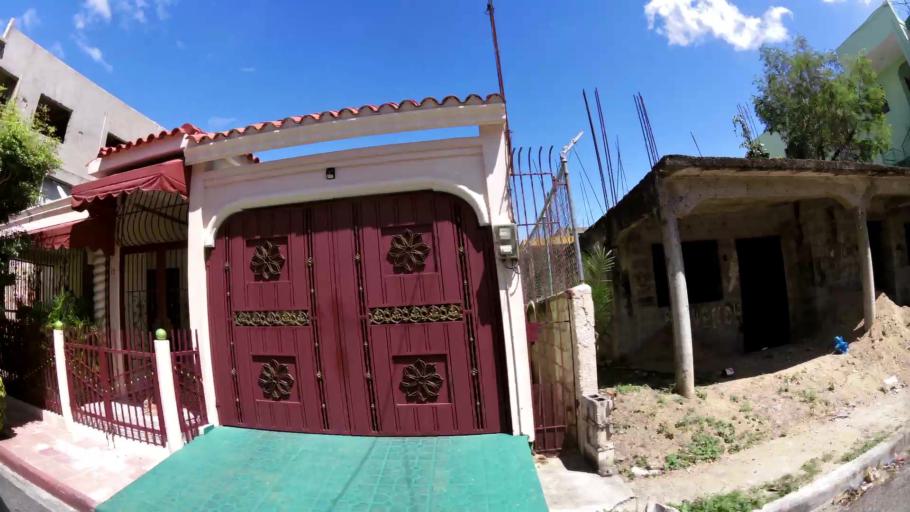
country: DO
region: San Cristobal
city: San Cristobal
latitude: 18.4148
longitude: -70.0906
